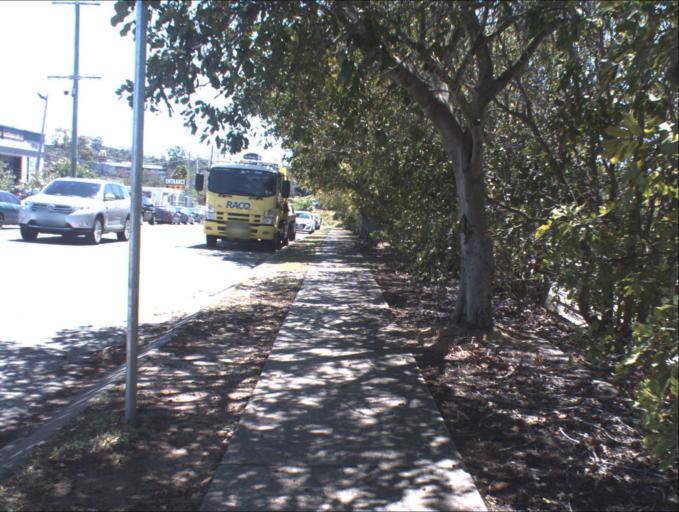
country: AU
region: Queensland
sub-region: Logan
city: Springwood
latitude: -27.6132
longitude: 153.1220
